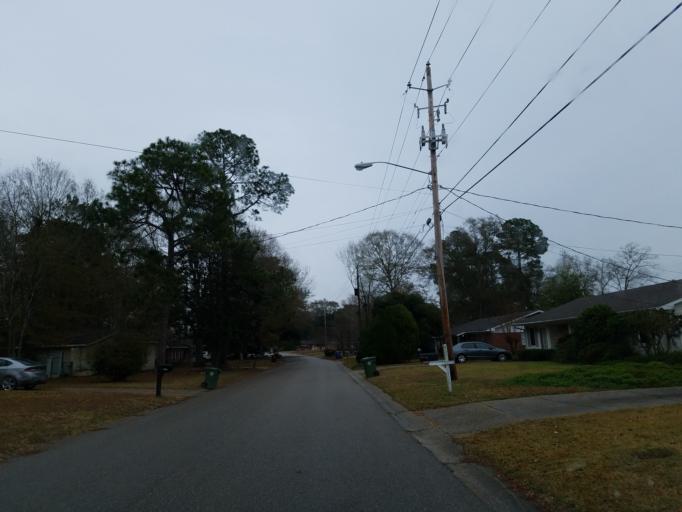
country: US
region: Mississippi
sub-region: Lamar County
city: West Hattiesburg
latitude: 31.3106
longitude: -89.3374
